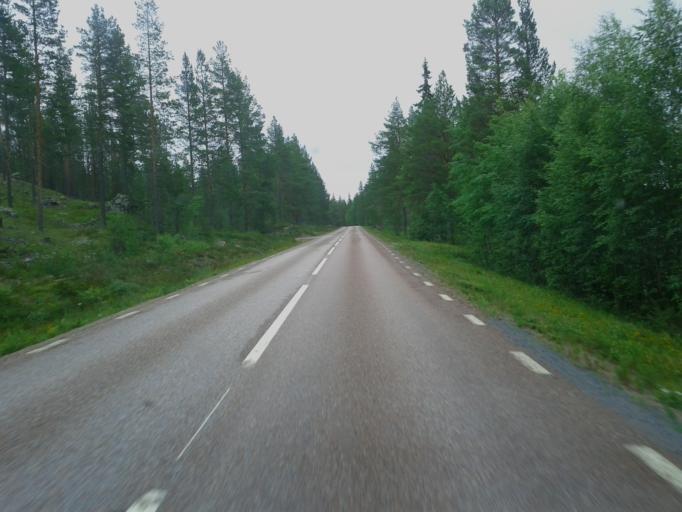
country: NO
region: Hedmark
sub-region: Trysil
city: Innbygda
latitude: 61.8338
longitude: 12.8349
